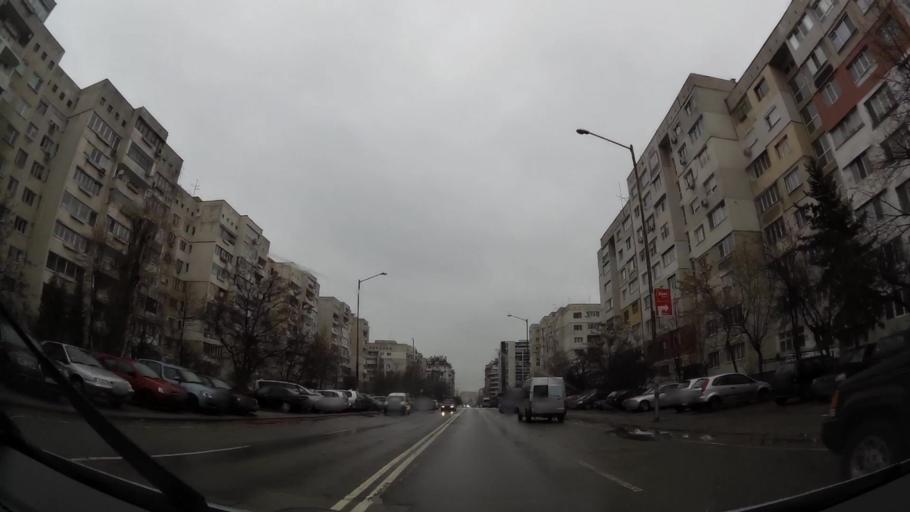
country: BG
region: Sofia-Capital
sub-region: Stolichna Obshtina
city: Sofia
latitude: 42.6316
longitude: 23.3750
